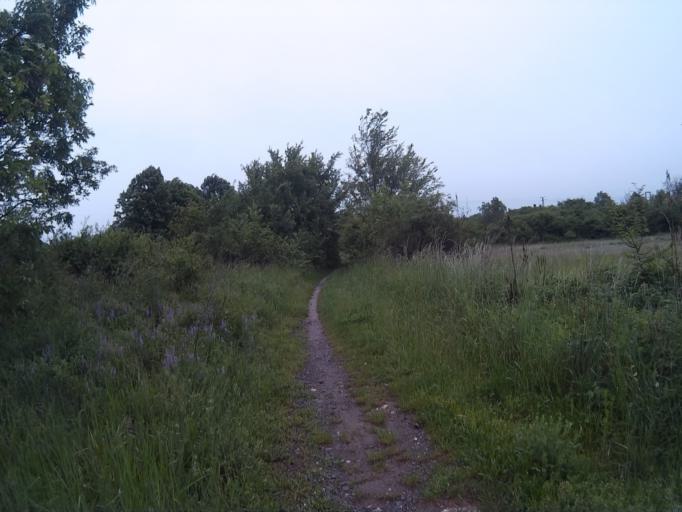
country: HU
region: Veszprem
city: Sumeg
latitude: 46.9660
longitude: 17.2927
